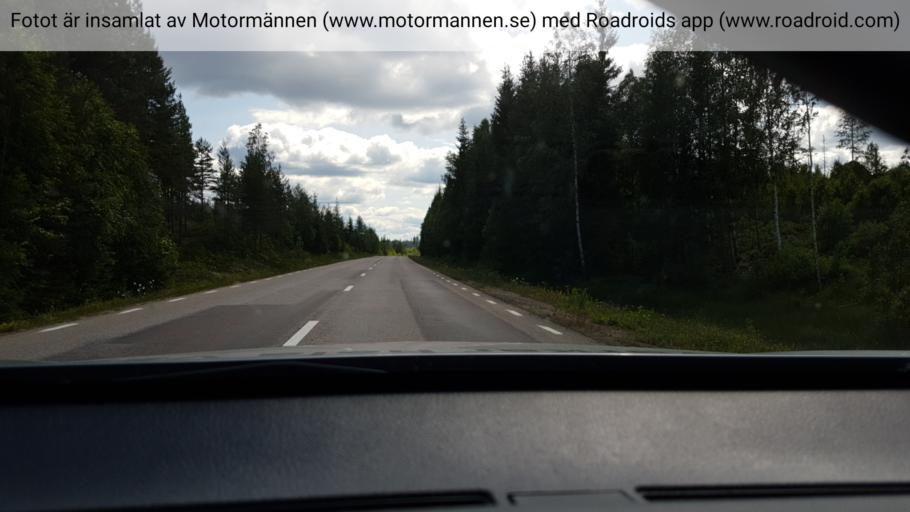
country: SE
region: Vaermland
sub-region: Filipstads Kommun
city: Lesjofors
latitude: 59.8929
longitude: 14.0072
